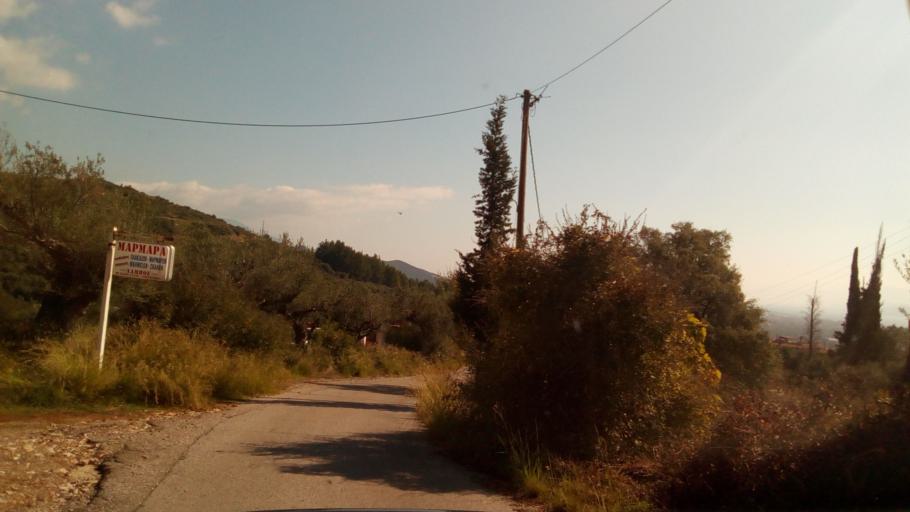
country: GR
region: West Greece
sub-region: Nomos Aitolias kai Akarnanias
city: Nafpaktos
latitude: 38.4200
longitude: 21.8693
